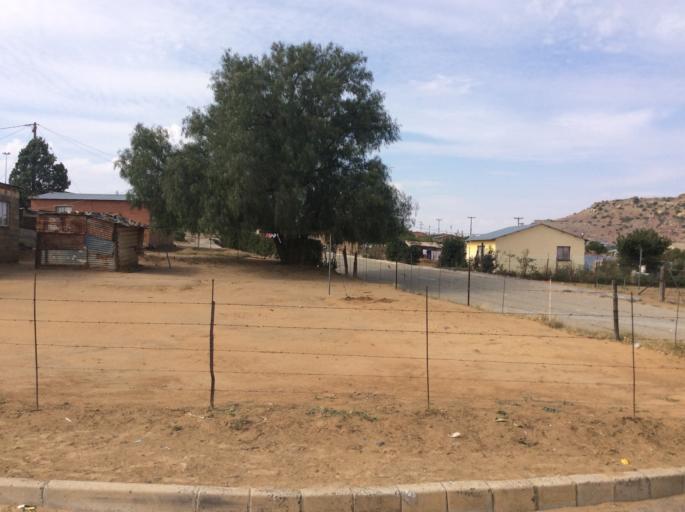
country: ZA
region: Orange Free State
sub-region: Xhariep District Municipality
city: Dewetsdorp
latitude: -29.5891
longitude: 26.6809
